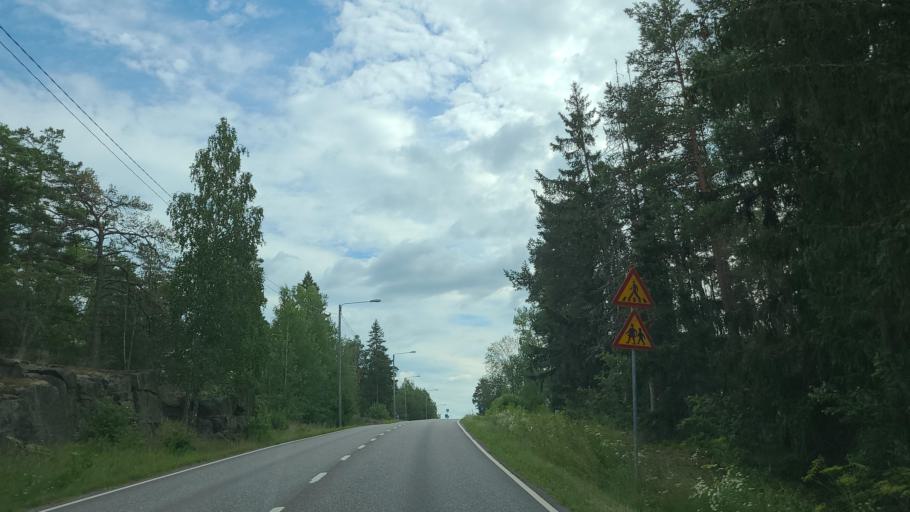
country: FI
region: Varsinais-Suomi
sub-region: Turku
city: Rymaettylae
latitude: 60.3751
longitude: 21.9468
